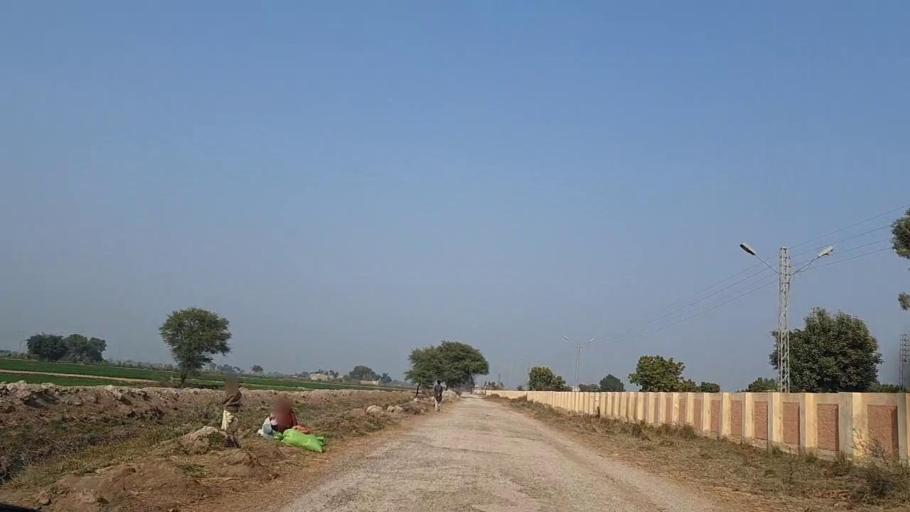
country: PK
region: Sindh
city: Sann
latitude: 26.1837
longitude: 68.1102
